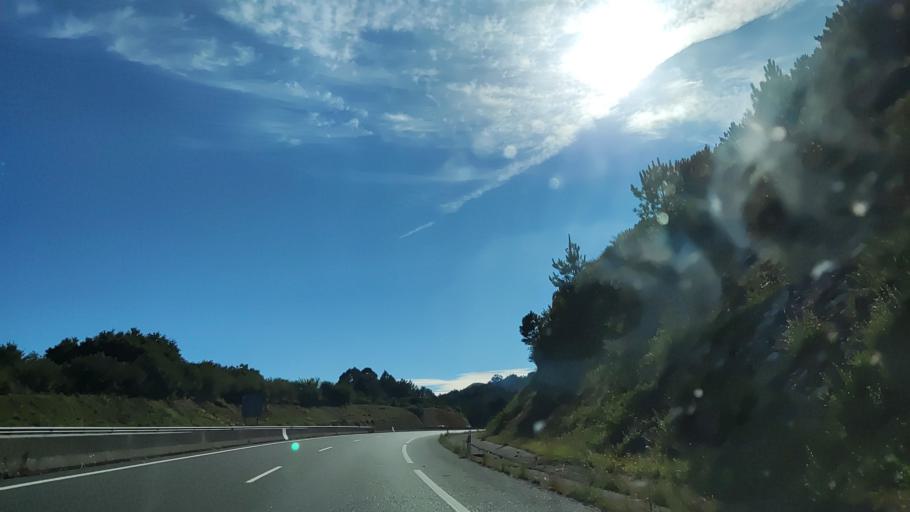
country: ES
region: Galicia
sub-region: Provincia da Coruna
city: Boiro
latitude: 42.6464
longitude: -8.9050
